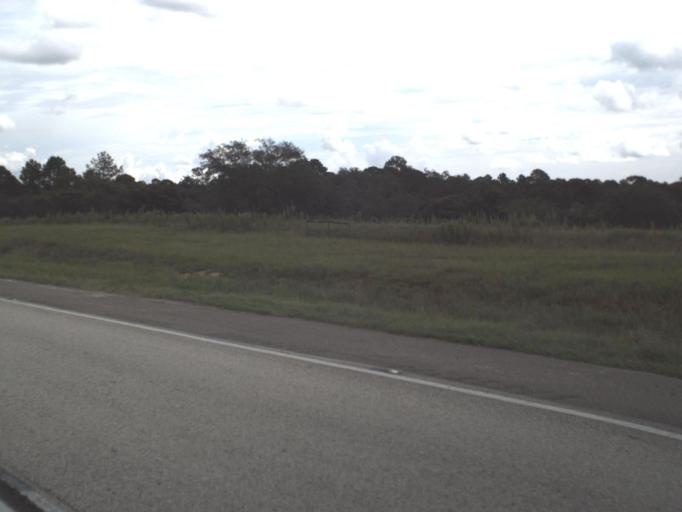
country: US
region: Florida
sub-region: Polk County
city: Loughman
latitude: 28.2387
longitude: -81.6411
